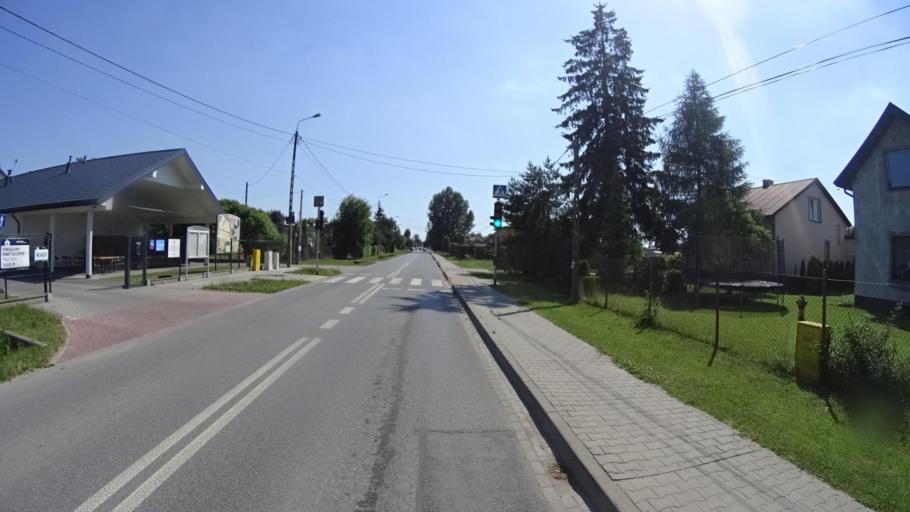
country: PL
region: Masovian Voivodeship
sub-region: Powiat warszawski zachodni
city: Bieniewice
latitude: 52.1949
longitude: 20.5304
